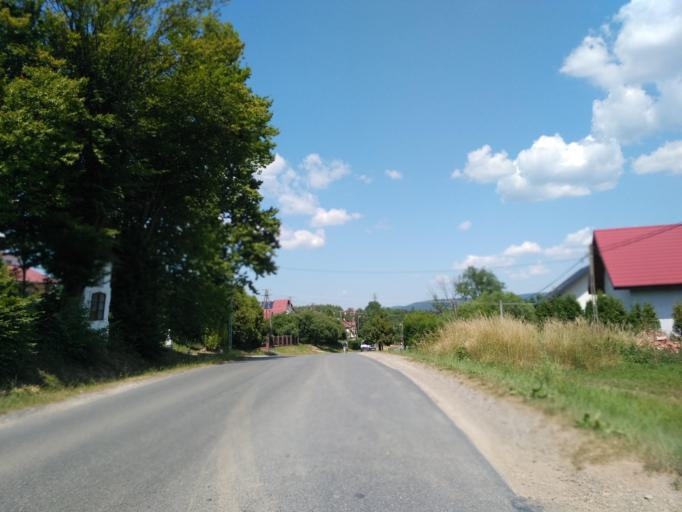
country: PL
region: Subcarpathian Voivodeship
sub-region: Powiat sanocki
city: Niebieszczany
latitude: 49.5514
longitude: 22.1434
